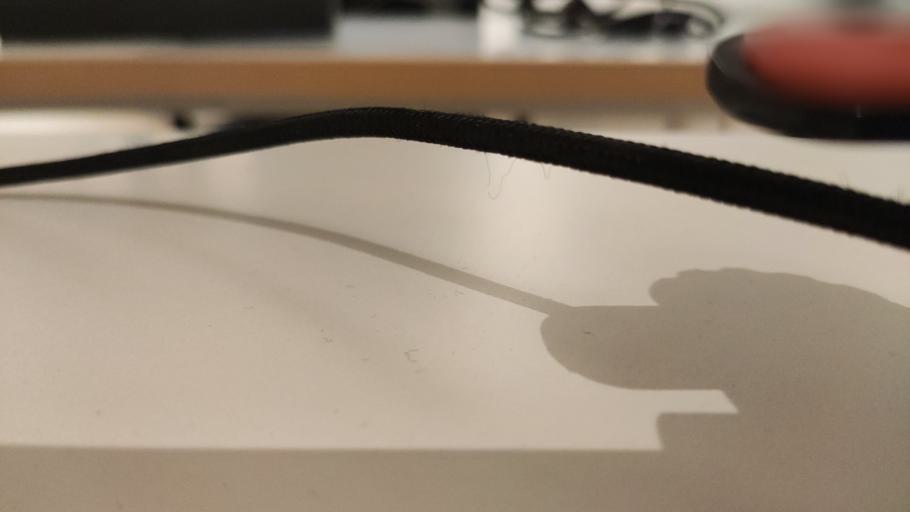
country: RU
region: Moskovskaya
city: Dorokhovo
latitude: 55.4313
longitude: 36.3524
